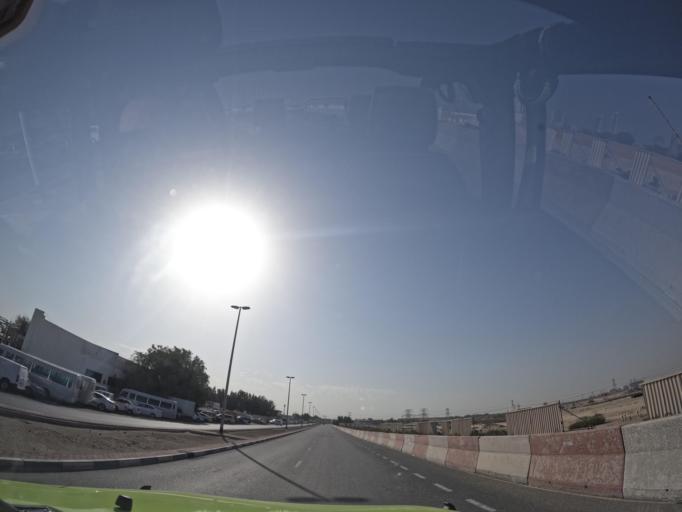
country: AE
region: Ash Shariqah
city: Sharjah
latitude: 25.1792
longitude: 55.3299
